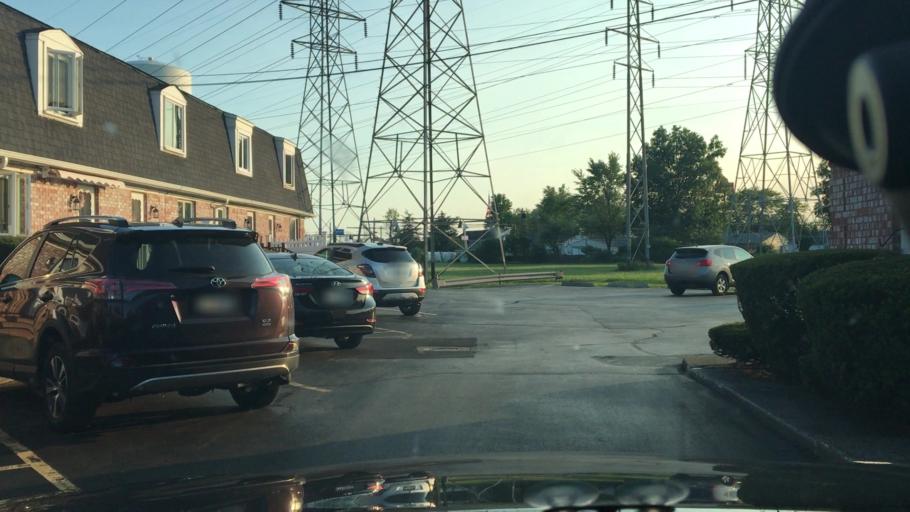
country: US
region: New York
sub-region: Erie County
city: Tonawanda
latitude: 43.0046
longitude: -78.8523
